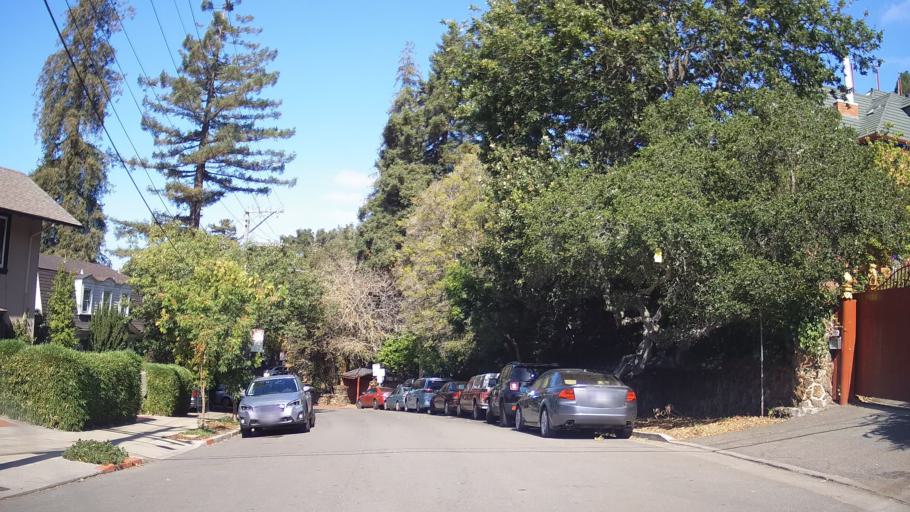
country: US
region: California
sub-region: Alameda County
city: Berkeley
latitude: 37.8667
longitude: -122.2485
